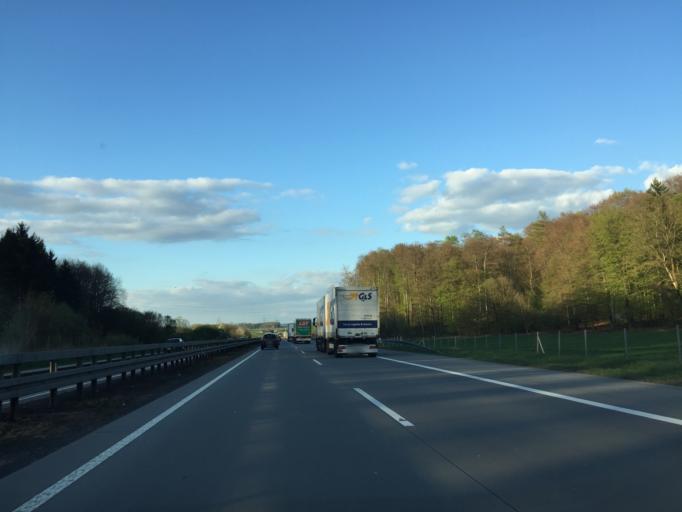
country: DE
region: Hesse
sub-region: Regierungsbezirk Giessen
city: Lich
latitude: 50.5395
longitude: 8.7762
